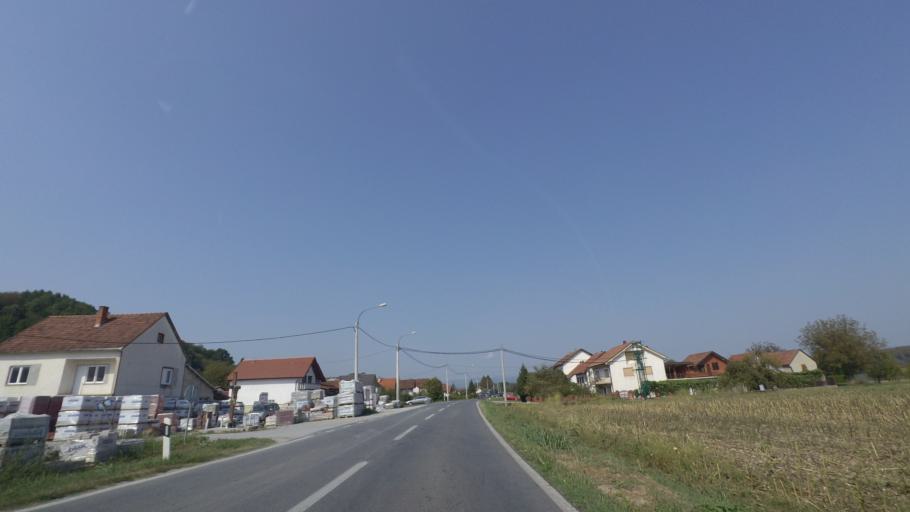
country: HR
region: Pozesko-Slavonska
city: Pozega
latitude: 45.3265
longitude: 17.6337
